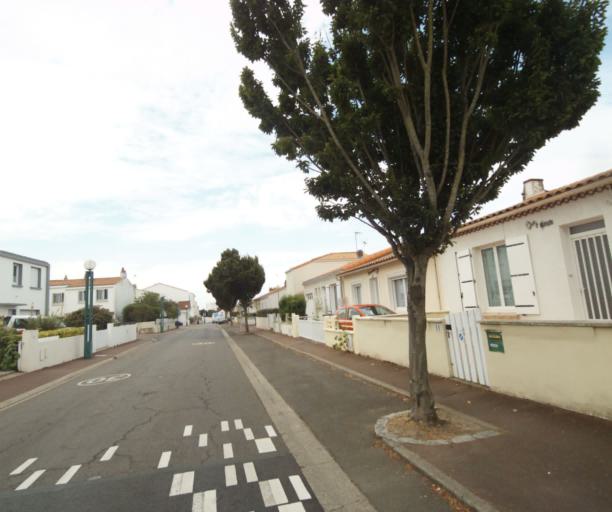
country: FR
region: Pays de la Loire
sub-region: Departement de la Vendee
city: Chateau-d'Olonne
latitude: 46.4941
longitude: -1.7591
